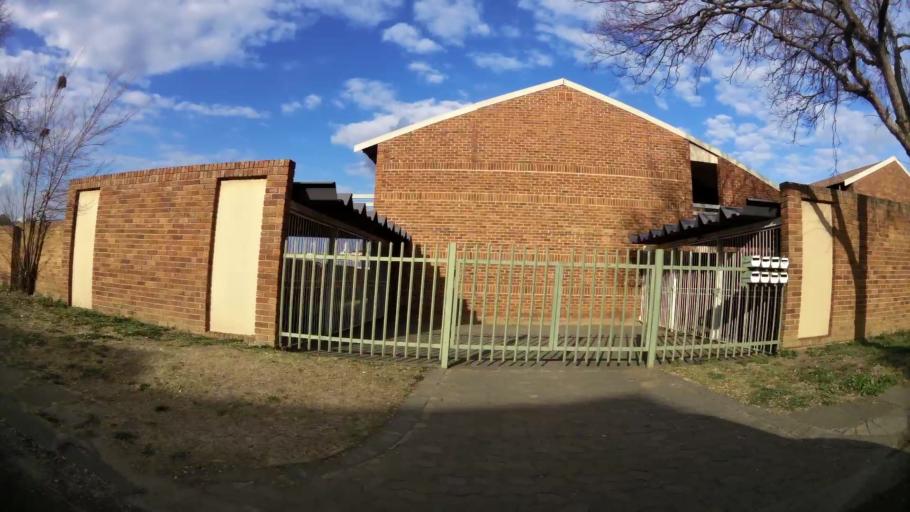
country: ZA
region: Orange Free State
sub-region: Mangaung Metropolitan Municipality
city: Bloemfontein
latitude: -29.1072
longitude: 26.1976
